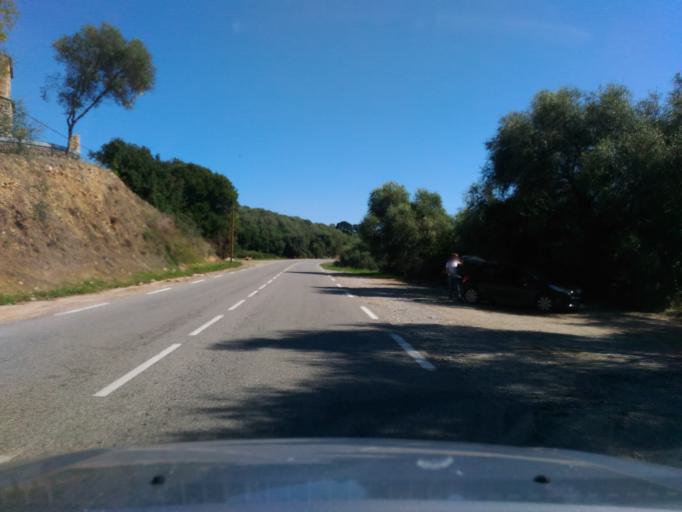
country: FR
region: Corsica
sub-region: Departement de la Haute-Corse
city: Aleria
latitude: 42.1140
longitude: 9.4952
